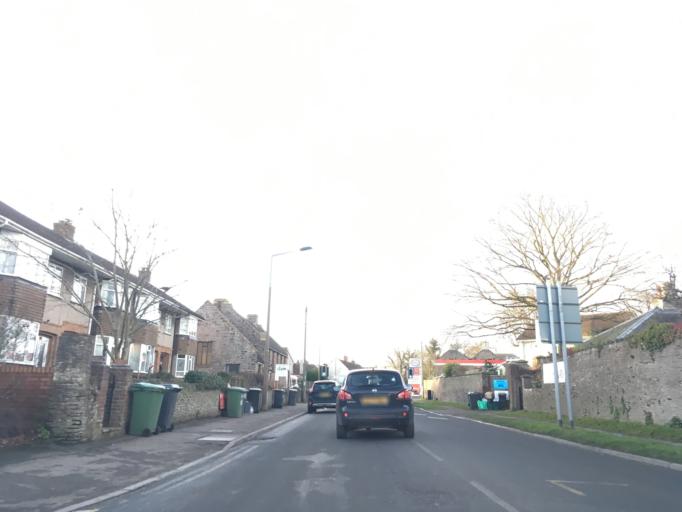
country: GB
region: England
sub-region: South Gloucestershire
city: Winterbourne
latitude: 51.5289
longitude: -2.5035
